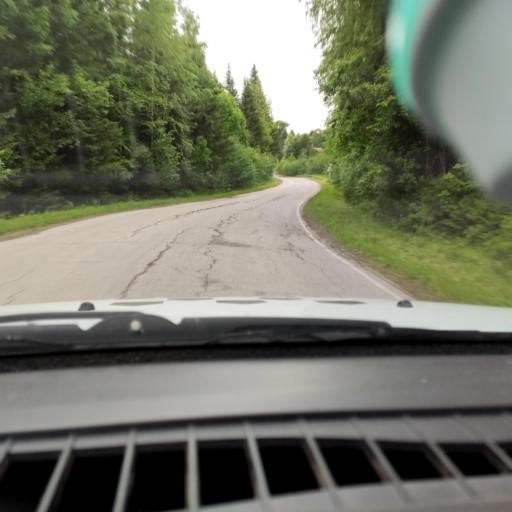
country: RU
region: Perm
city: Lys'va
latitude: 58.1155
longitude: 57.6986
